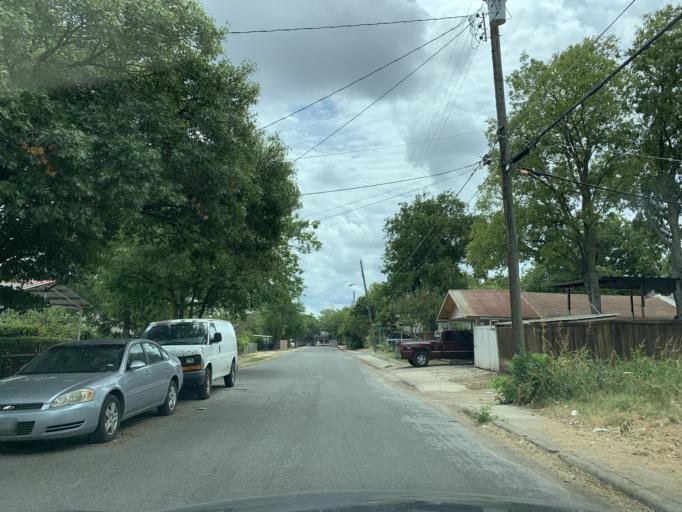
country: US
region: Texas
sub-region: Dallas County
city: Cockrell Hill
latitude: 32.7438
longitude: -96.8773
